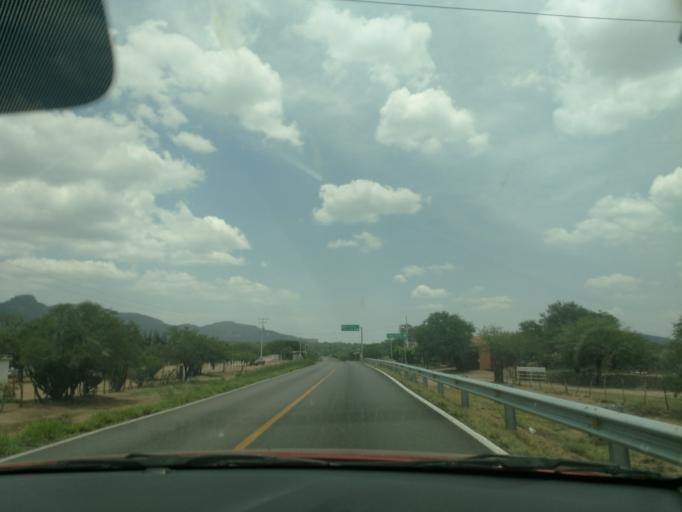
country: MX
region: San Luis Potosi
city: Villa Juarez
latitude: 22.0185
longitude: -100.3874
